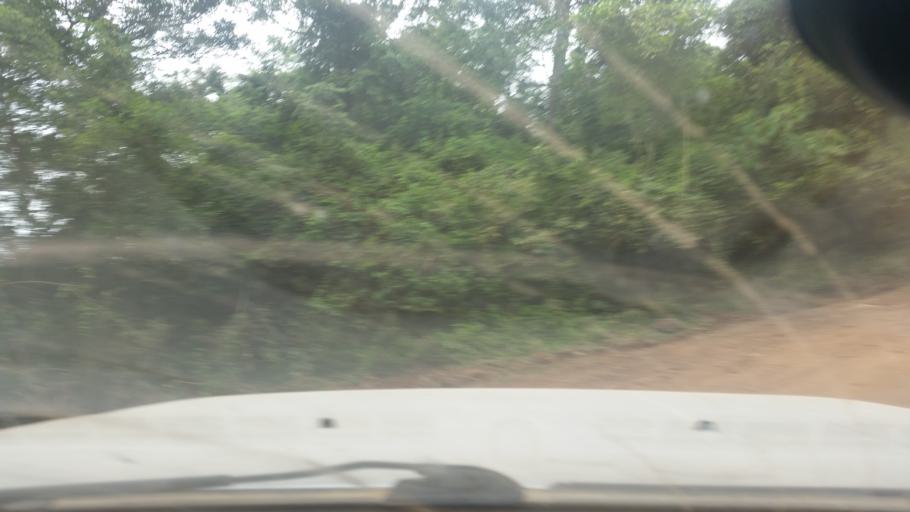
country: PY
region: Guaira
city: Independencia
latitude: -25.8200
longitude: -56.2742
